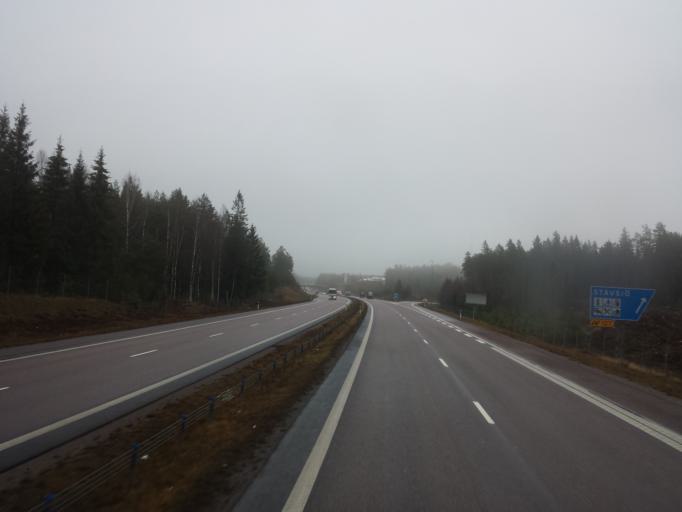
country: SE
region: OEstergoetland
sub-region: Norrkopings Kommun
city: Krokek
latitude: 58.7259
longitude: 16.3997
